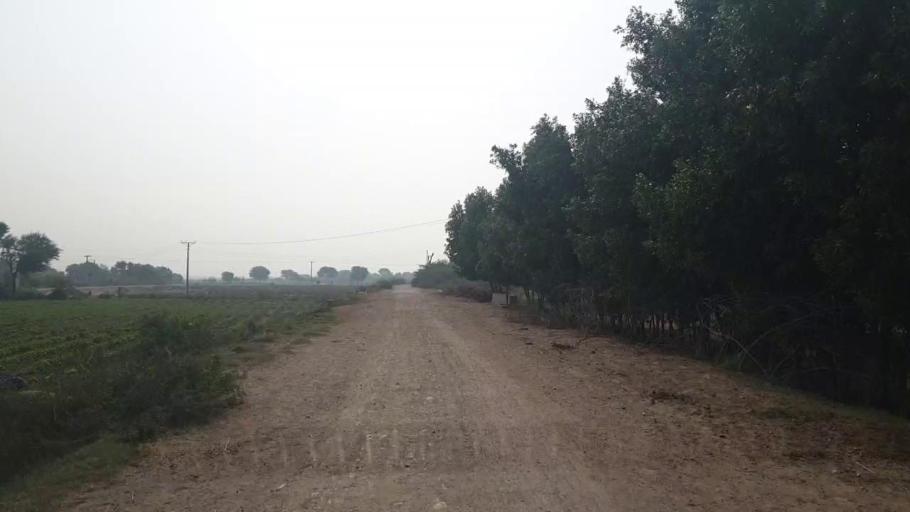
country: PK
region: Sindh
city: Tando Muhammad Khan
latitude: 25.2654
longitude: 68.5108
